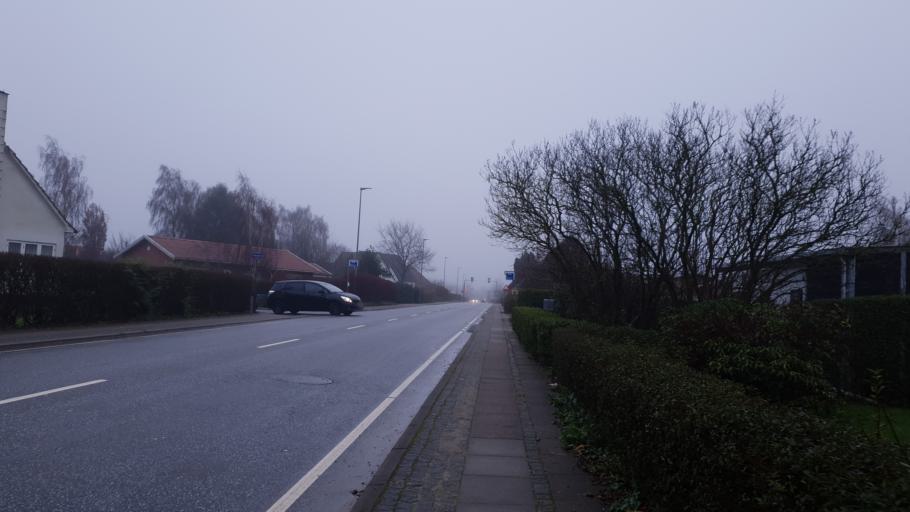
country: DK
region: Central Jutland
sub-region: Hedensted Kommune
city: Hedensted
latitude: 55.8019
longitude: 9.6944
